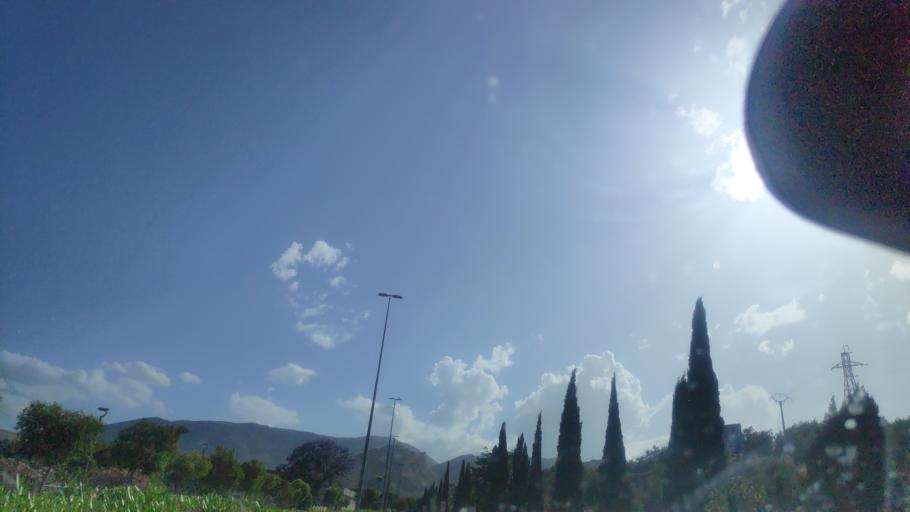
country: ES
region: Andalusia
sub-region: Provincia de Jaen
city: Jaen
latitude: 37.7716
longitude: -3.7739
